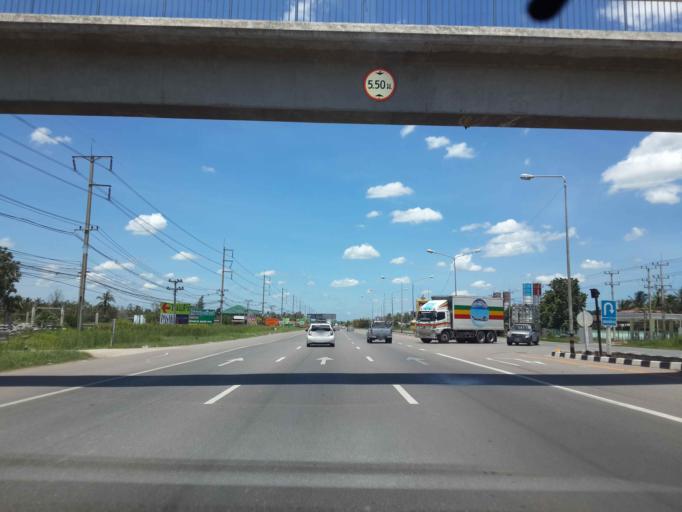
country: TH
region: Samut Songkhram
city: Amphawa
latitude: 13.3732
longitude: 99.9608
